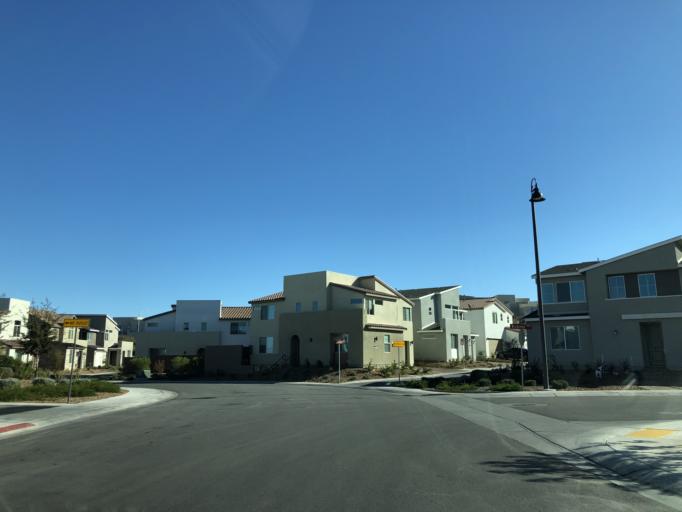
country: US
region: Nevada
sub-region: Clark County
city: Whitney
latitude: 35.9998
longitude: -115.0848
